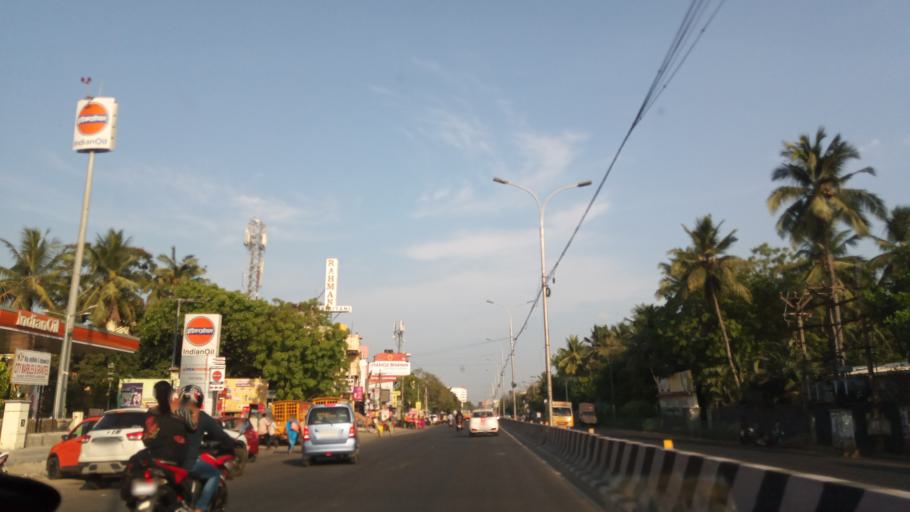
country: IN
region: Tamil Nadu
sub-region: Kancheepuram
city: Manappakkam
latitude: 13.0259
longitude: 80.1750
